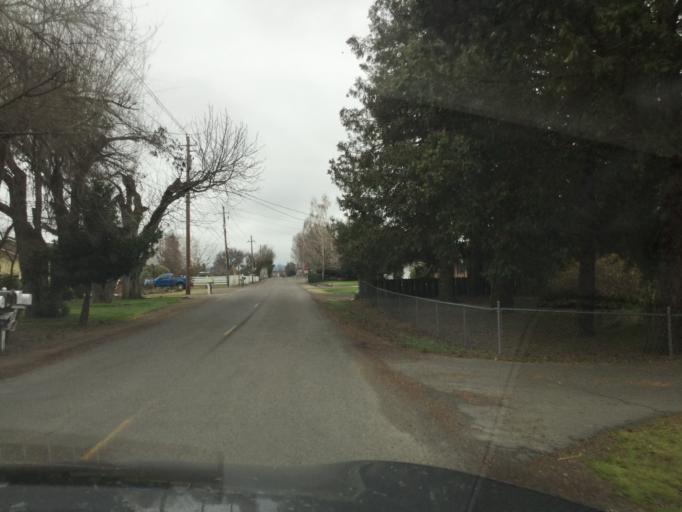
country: US
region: Oregon
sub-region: Jackson County
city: Central Point
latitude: 42.3925
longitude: -122.9188
